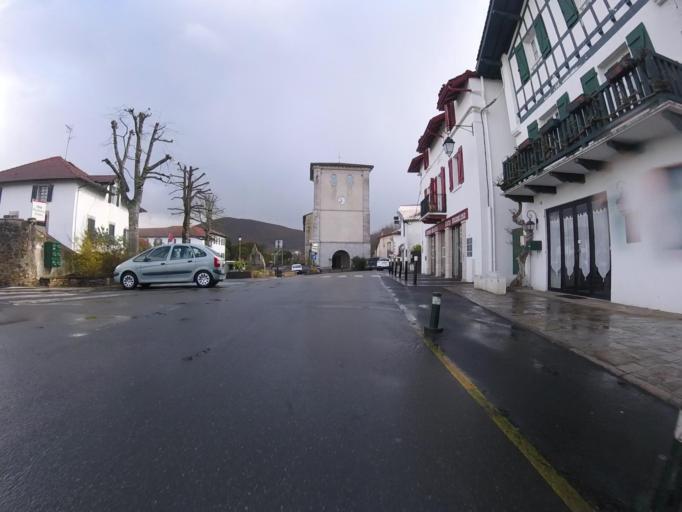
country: FR
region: Aquitaine
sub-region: Departement des Pyrenees-Atlantiques
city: Ascain
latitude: 43.3448
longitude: -1.6214
